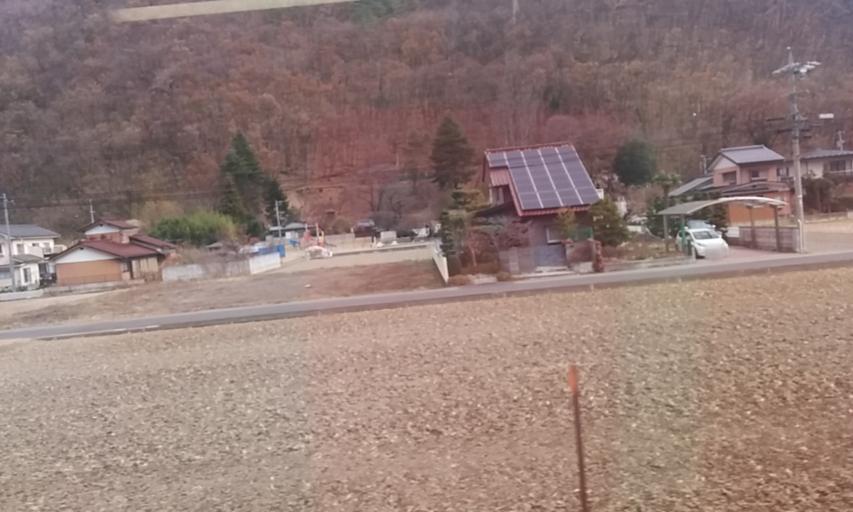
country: JP
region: Nagano
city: Ueda
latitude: 36.4881
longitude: 138.1547
